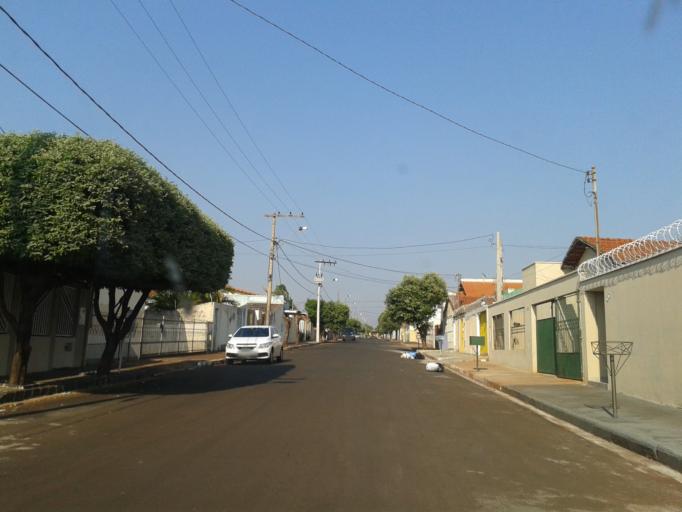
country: BR
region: Minas Gerais
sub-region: Ituiutaba
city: Ituiutaba
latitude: -18.9749
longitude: -49.4735
